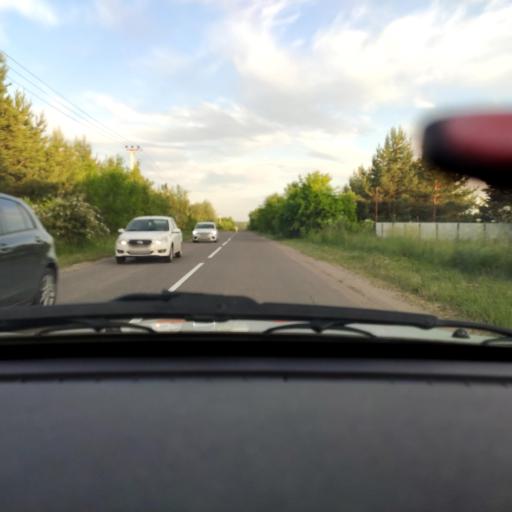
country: RU
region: Voronezj
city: Podgornoye
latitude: 51.8358
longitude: 39.2018
